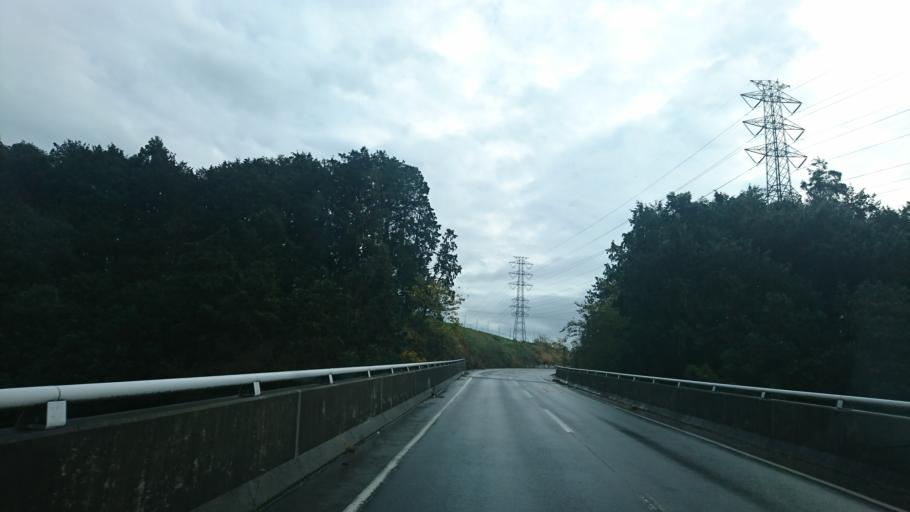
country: JP
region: Shizuoka
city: Fuji
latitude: 35.1723
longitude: 138.7321
